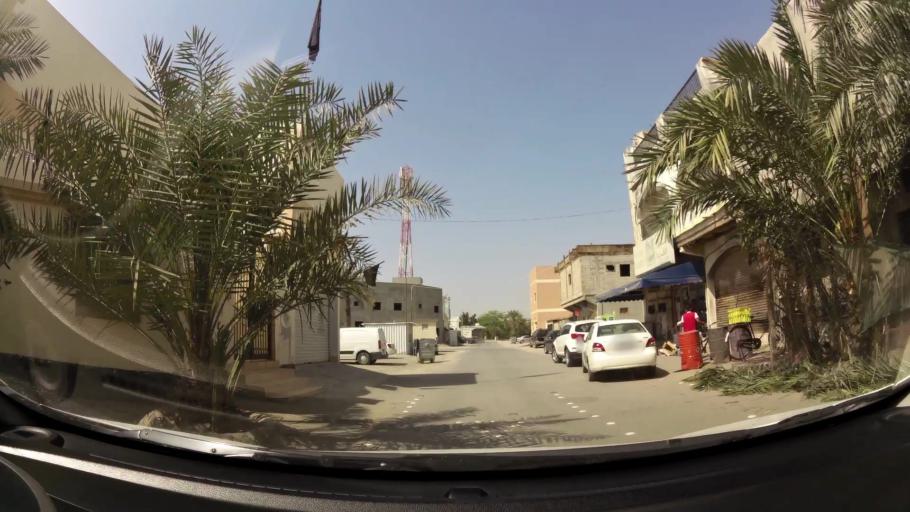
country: BH
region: Manama
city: Jidd Hafs
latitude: 26.1963
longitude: 50.4647
